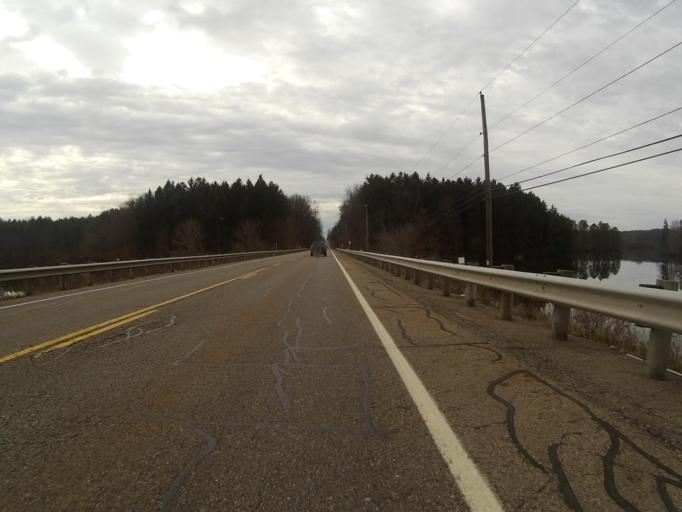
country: US
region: Ohio
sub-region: Portage County
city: Brimfield
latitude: 41.0596
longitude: -81.3473
